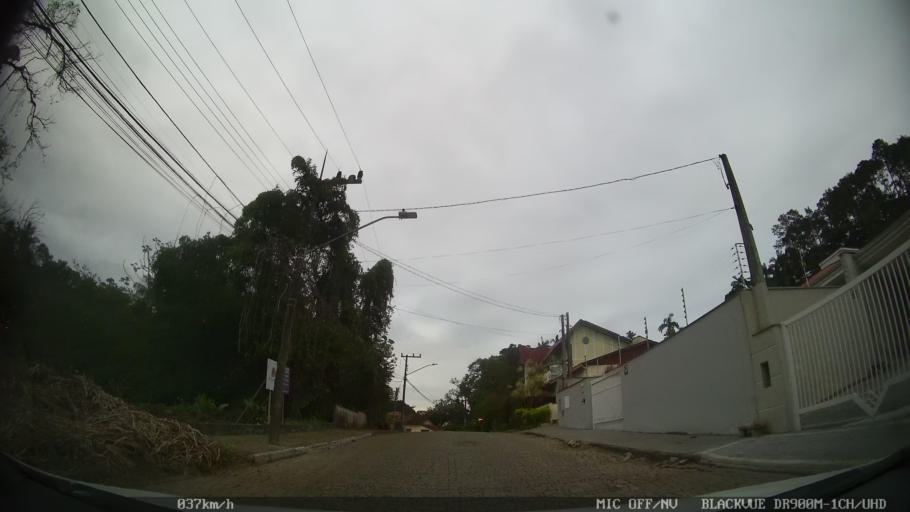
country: BR
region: Santa Catarina
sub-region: Joinville
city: Joinville
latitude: -26.2973
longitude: -48.8589
